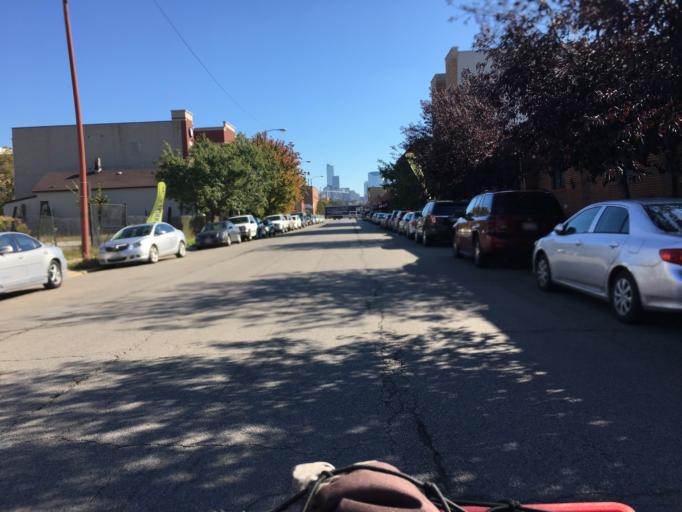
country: US
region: Illinois
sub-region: Cook County
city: Chicago
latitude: 41.8868
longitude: -87.6764
